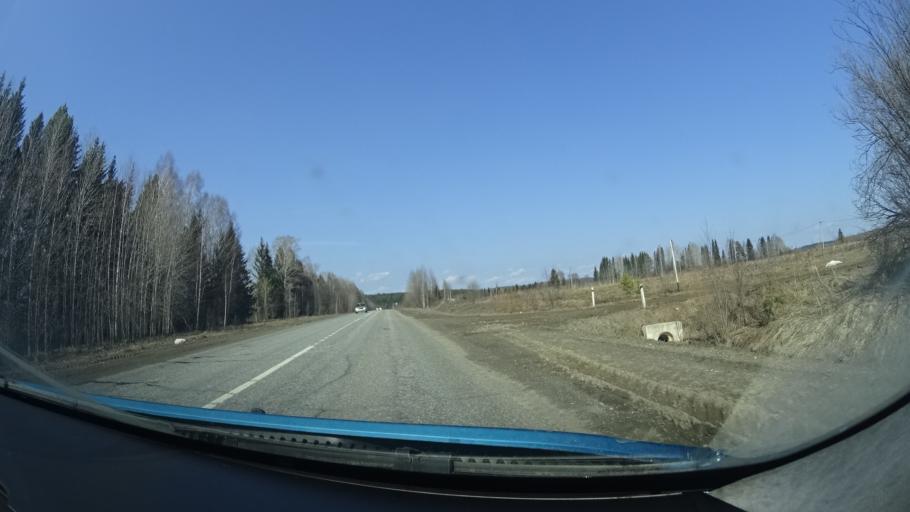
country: RU
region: Perm
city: Yugo-Kamskiy
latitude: 57.5370
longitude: 55.6884
